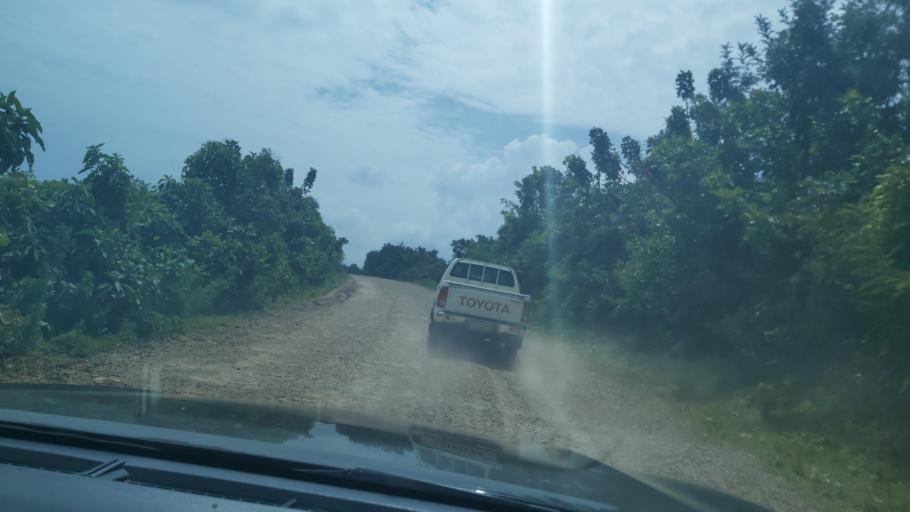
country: ET
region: Oromiya
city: Jima
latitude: 7.7409
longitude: 36.7884
